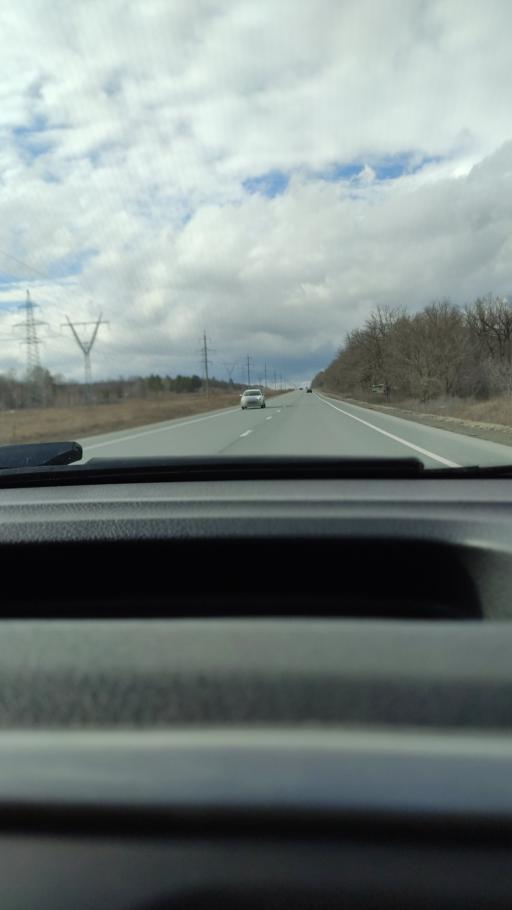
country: RU
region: Samara
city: Bogatyr'
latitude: 53.4957
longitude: 49.9630
